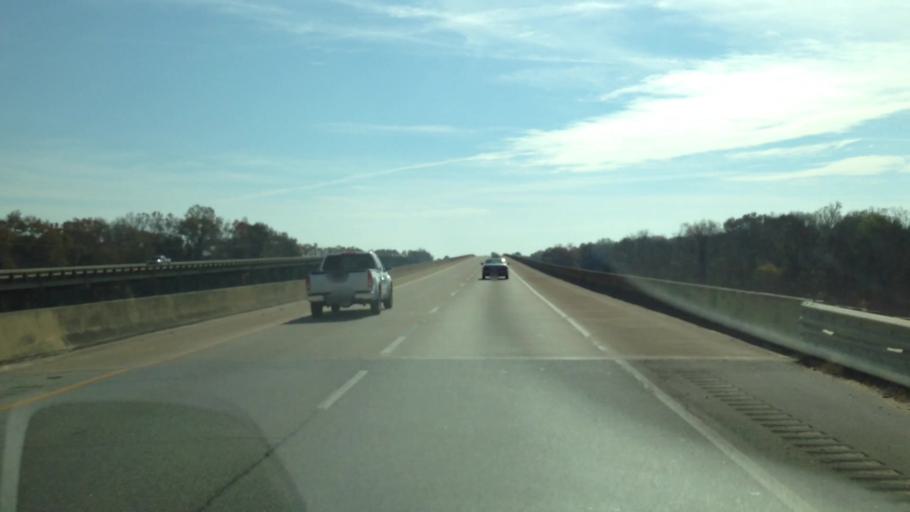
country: US
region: Alabama
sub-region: Autauga County
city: Prattville
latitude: 32.4155
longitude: -86.4098
